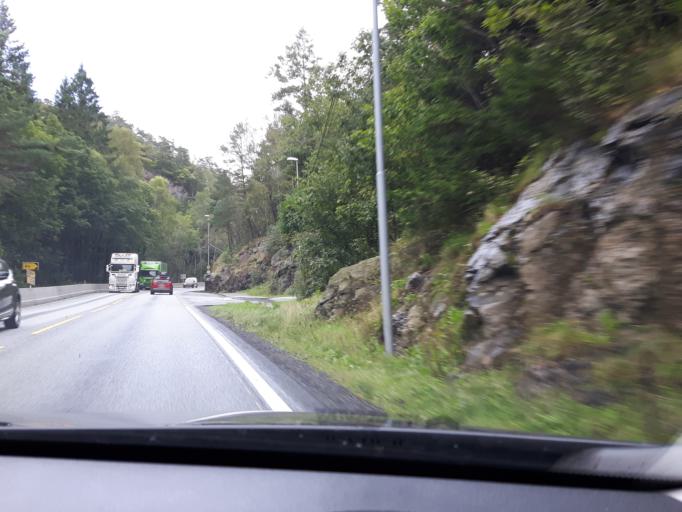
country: NO
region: Vest-Agder
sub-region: Marnardal
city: Helland
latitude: 58.0807
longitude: 7.6147
